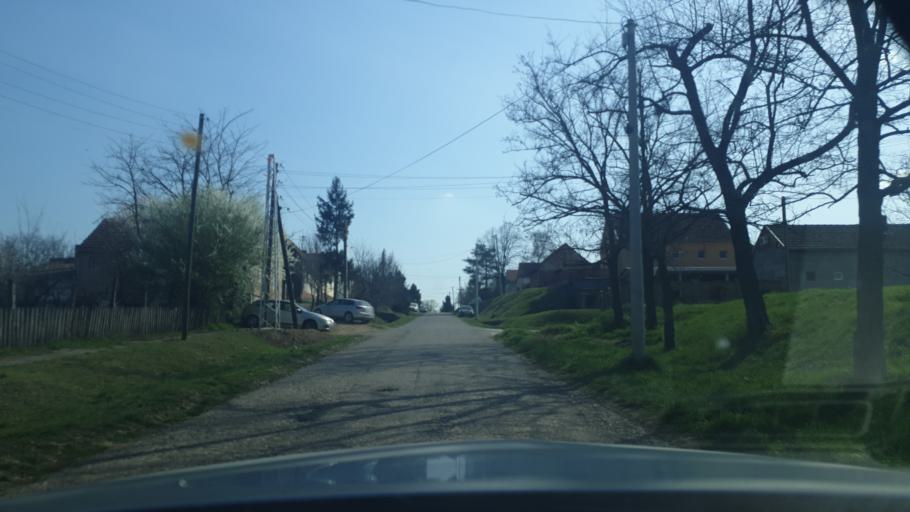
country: RS
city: Putinci
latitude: 45.0059
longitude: 19.9391
